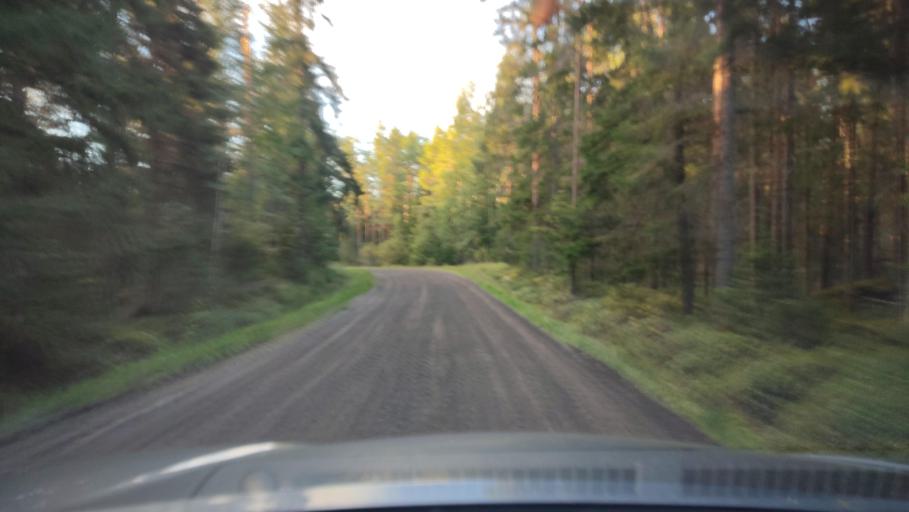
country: FI
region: Southern Ostrobothnia
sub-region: Suupohja
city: Karijoki
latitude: 62.2312
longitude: 21.5735
